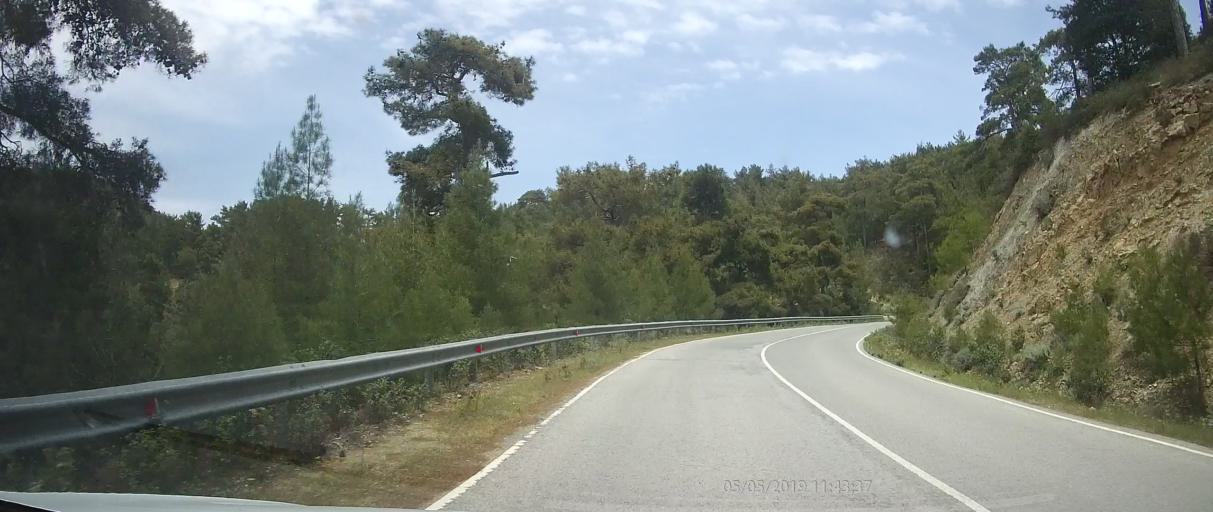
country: CY
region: Lefkosia
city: Kato Pyrgos
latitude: 35.0084
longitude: 32.6697
